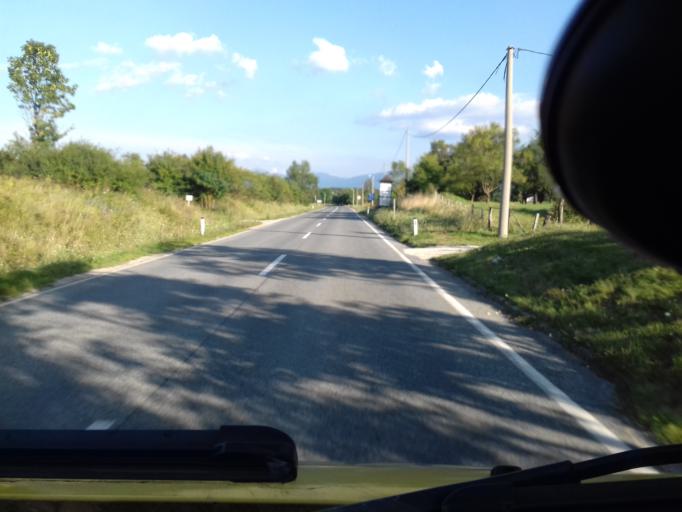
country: BA
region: Federation of Bosnia and Herzegovina
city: Orasac
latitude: 44.6390
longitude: 16.1720
